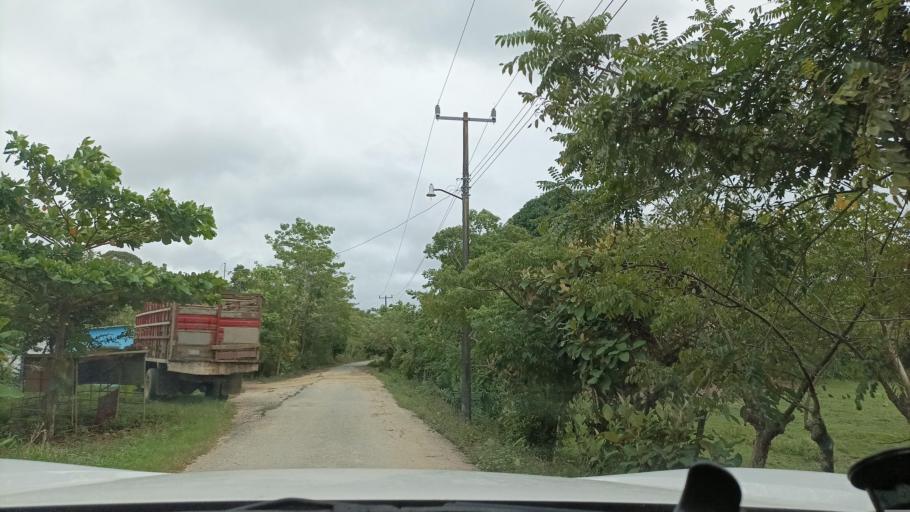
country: MX
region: Veracruz
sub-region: Moloacan
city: Cuichapa
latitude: 17.8536
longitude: -94.3560
